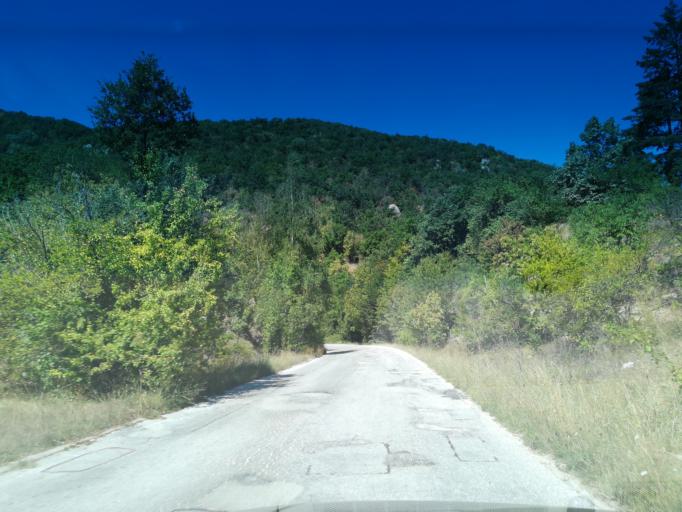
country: BG
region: Pazardzhik
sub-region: Obshtina Strelcha
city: Strelcha
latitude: 42.5484
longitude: 24.3299
